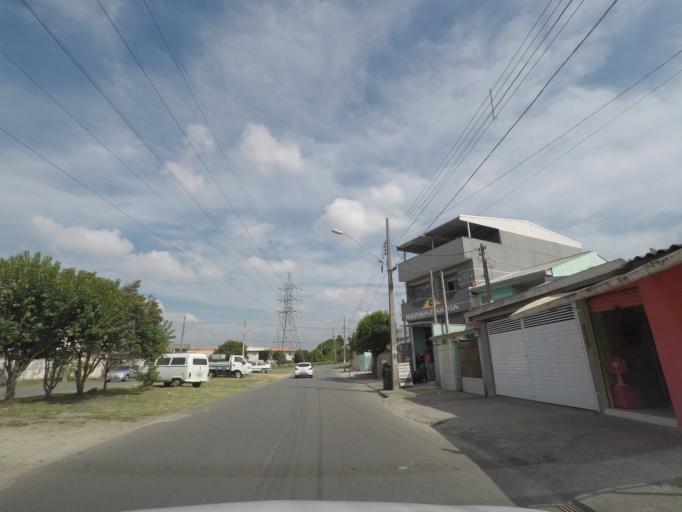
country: BR
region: Parana
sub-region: Pinhais
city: Pinhais
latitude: -25.4662
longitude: -49.1972
